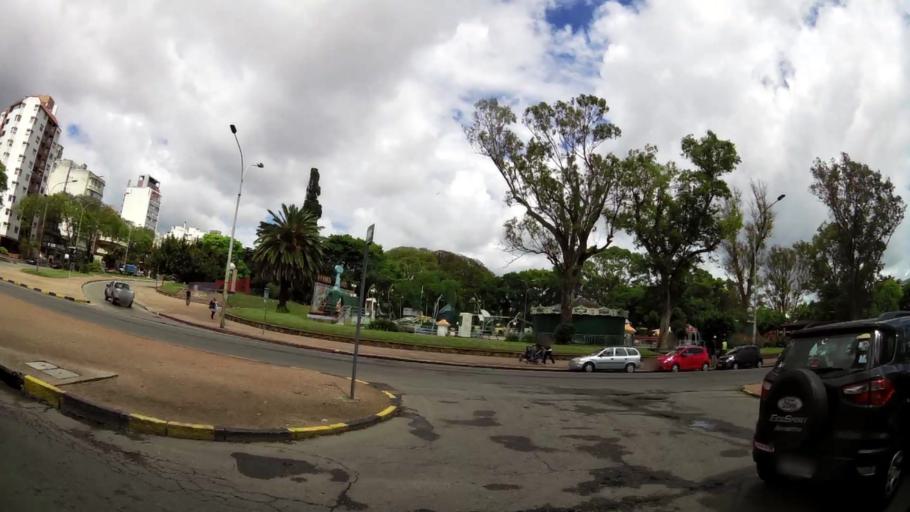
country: UY
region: Montevideo
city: Montevideo
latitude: -34.9134
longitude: -56.1629
